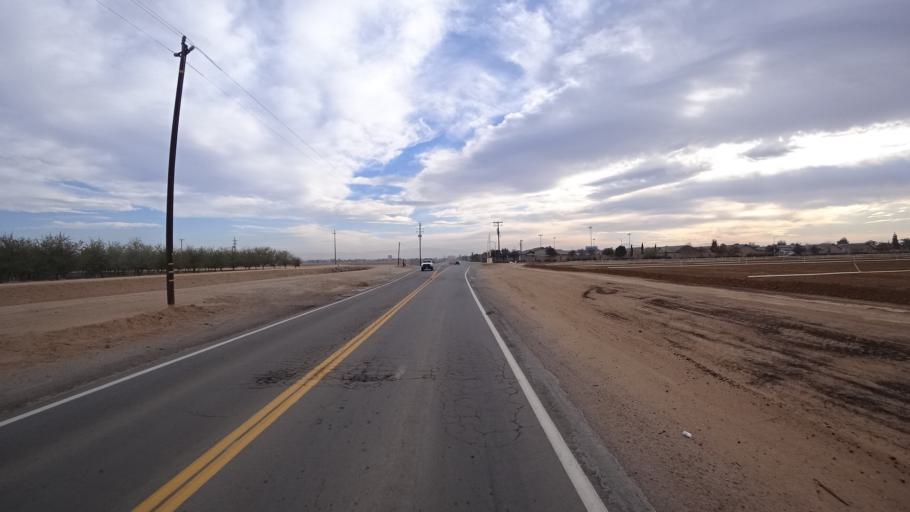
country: US
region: California
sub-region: Kern County
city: Rosedale
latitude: 35.4197
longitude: -119.1556
